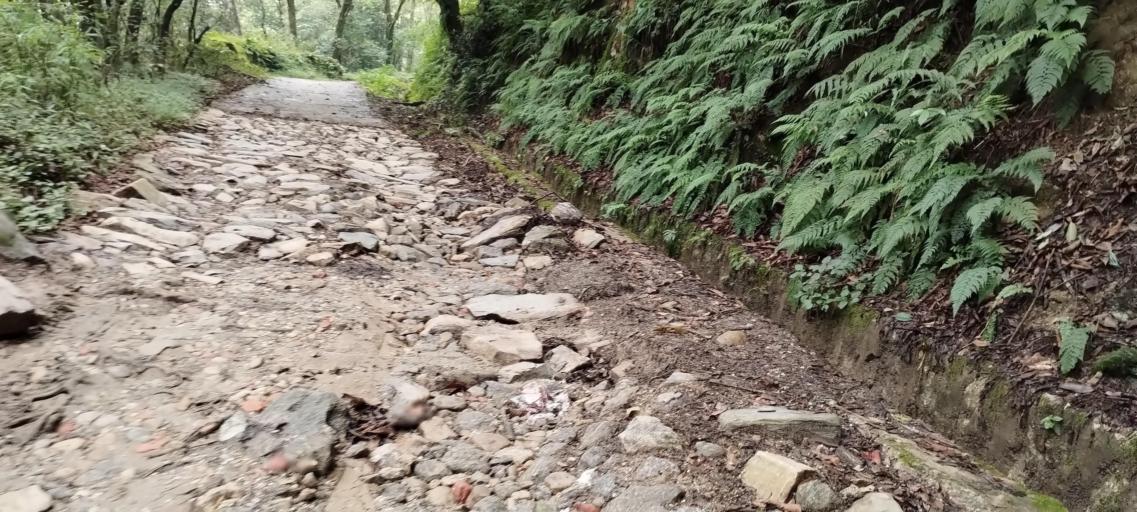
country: NP
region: Central Region
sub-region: Bagmati Zone
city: Kathmandu
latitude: 27.7912
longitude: 85.3737
